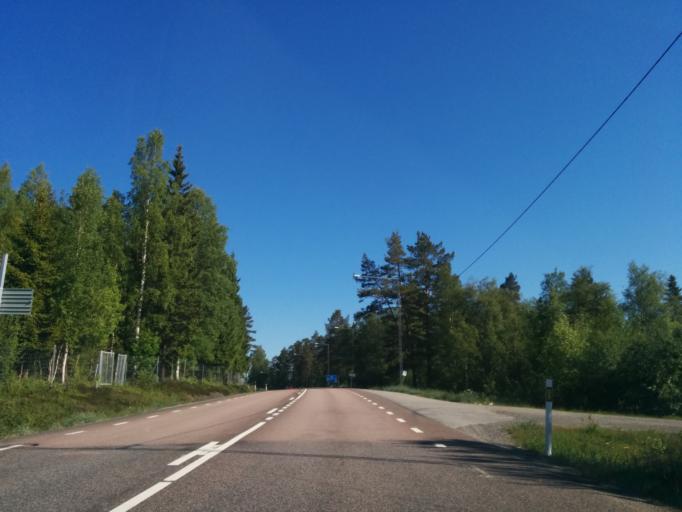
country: SE
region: Vaesternorrland
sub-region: Haernoesands Kommun
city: Haernoesand
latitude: 62.7869
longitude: 17.9179
